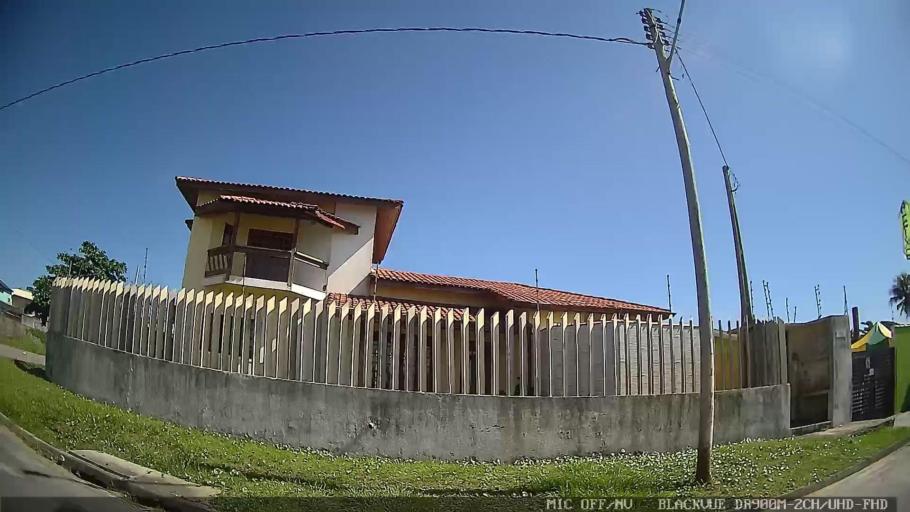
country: BR
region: Sao Paulo
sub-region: Peruibe
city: Peruibe
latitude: -24.2820
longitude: -46.9447
